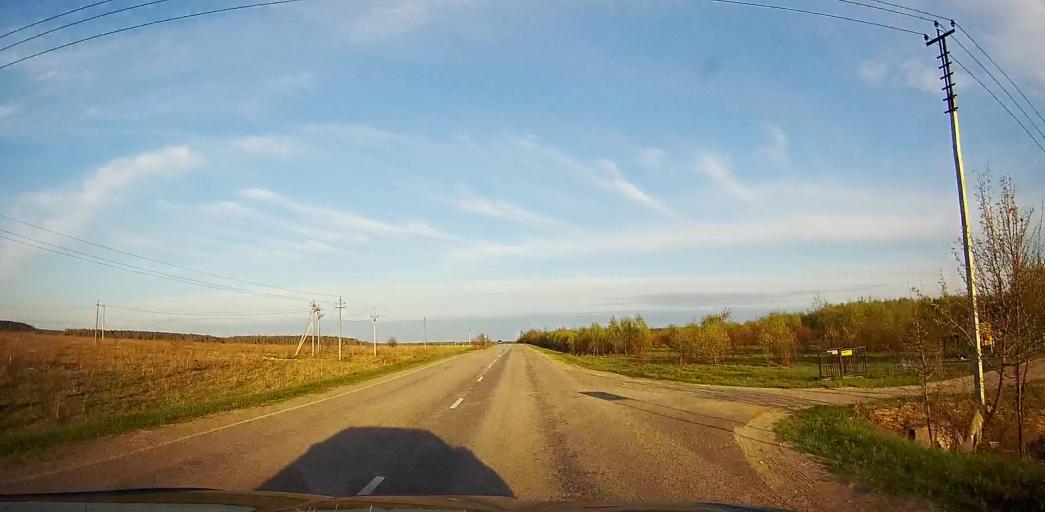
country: RU
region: Moskovskaya
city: Meshcherino
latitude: 55.2439
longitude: 38.3263
